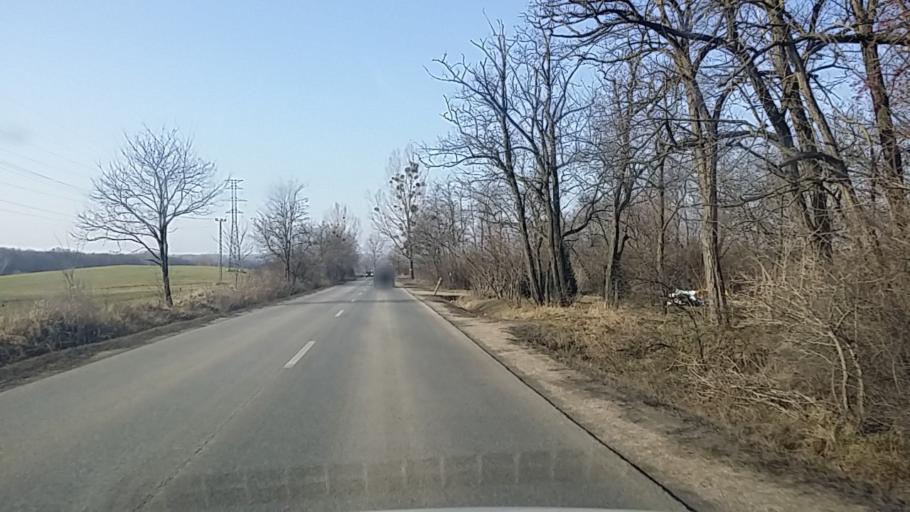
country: HU
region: Komarom-Esztergom
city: Oroszlany
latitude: 47.4750
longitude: 18.2893
